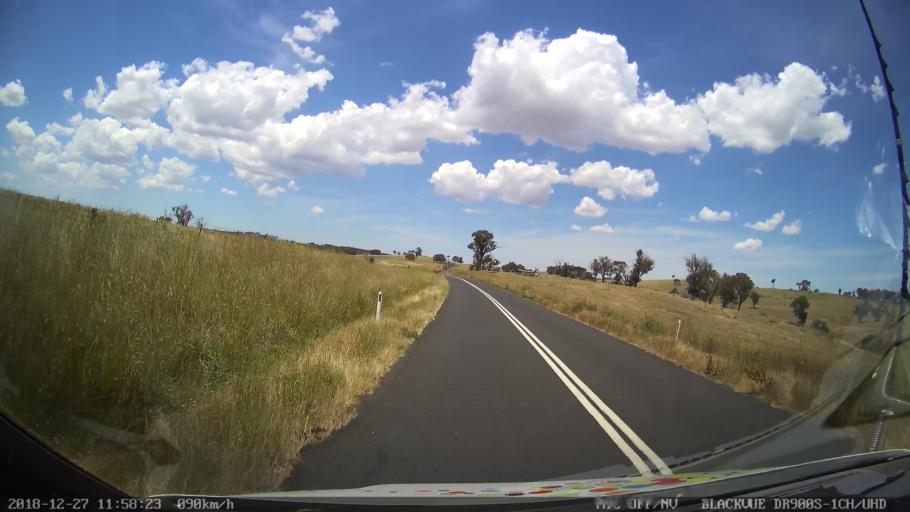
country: AU
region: New South Wales
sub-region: Blayney
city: Blayney
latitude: -33.7232
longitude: 149.3839
